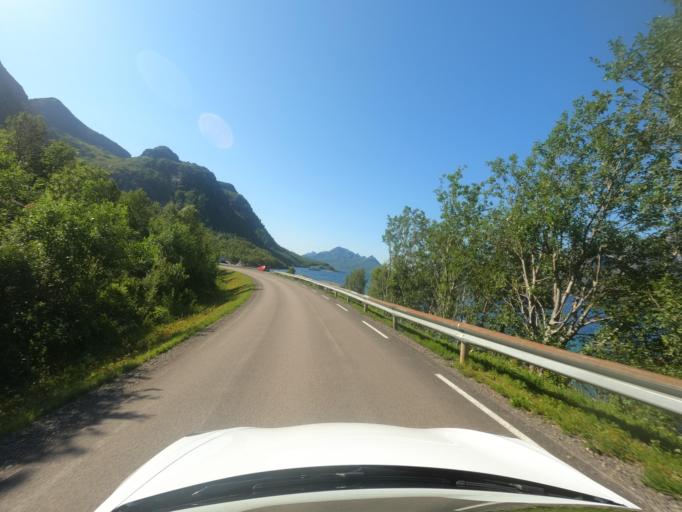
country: NO
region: Nordland
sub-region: Hadsel
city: Stokmarknes
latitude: 68.3459
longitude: 15.0517
